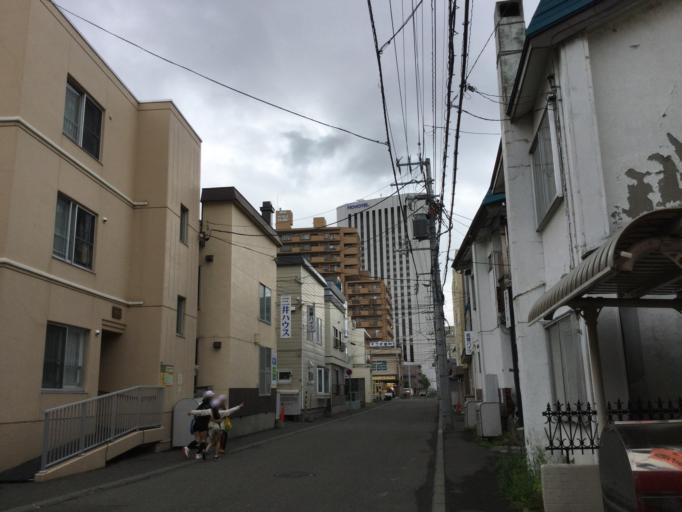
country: JP
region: Hokkaido
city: Sapporo
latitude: 43.0474
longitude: 141.3487
